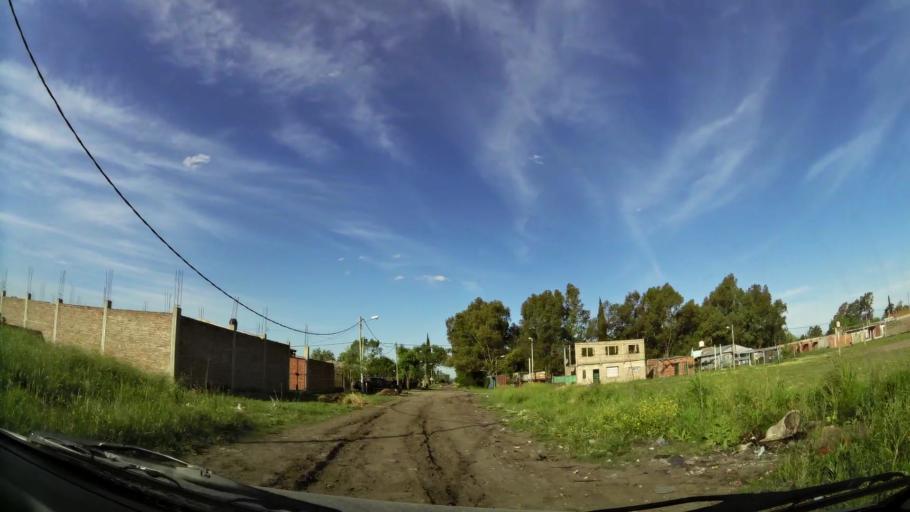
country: AR
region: Buenos Aires
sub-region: Partido de Almirante Brown
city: Adrogue
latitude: -34.8152
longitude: -58.3237
